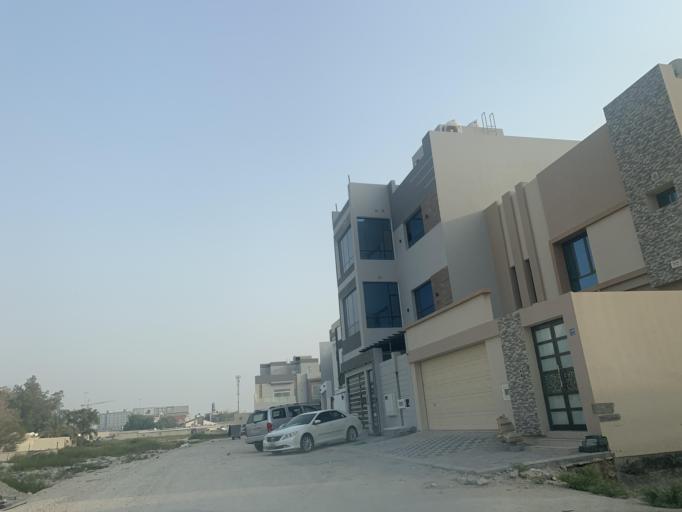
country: BH
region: Manama
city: Jidd Hafs
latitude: 26.2214
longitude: 50.5200
